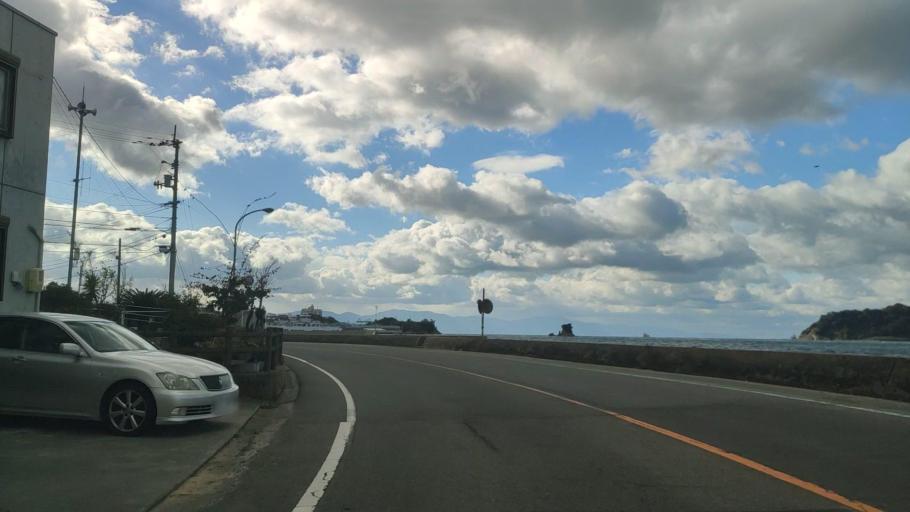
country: JP
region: Ehime
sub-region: Shikoku-chuo Shi
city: Matsuyama
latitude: 33.8862
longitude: 132.7008
